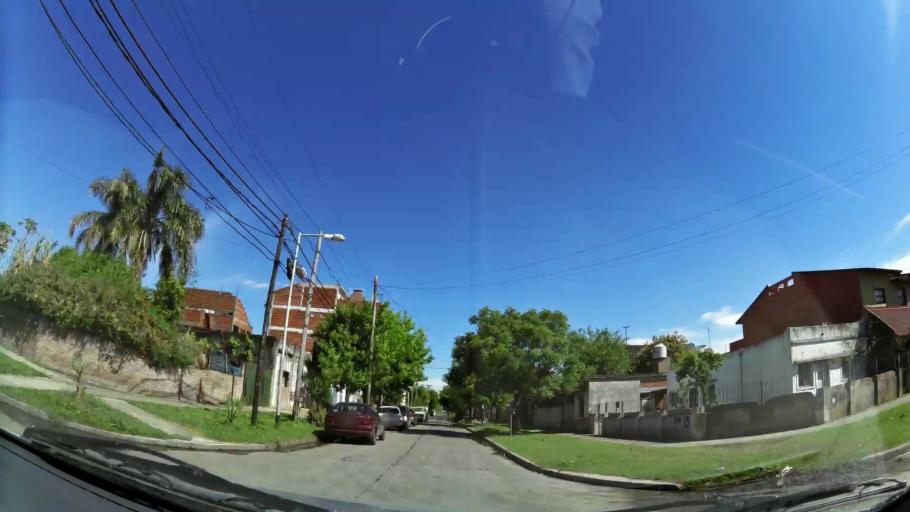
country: AR
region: Buenos Aires
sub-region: Partido de Quilmes
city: Quilmes
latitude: -34.6915
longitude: -58.3069
